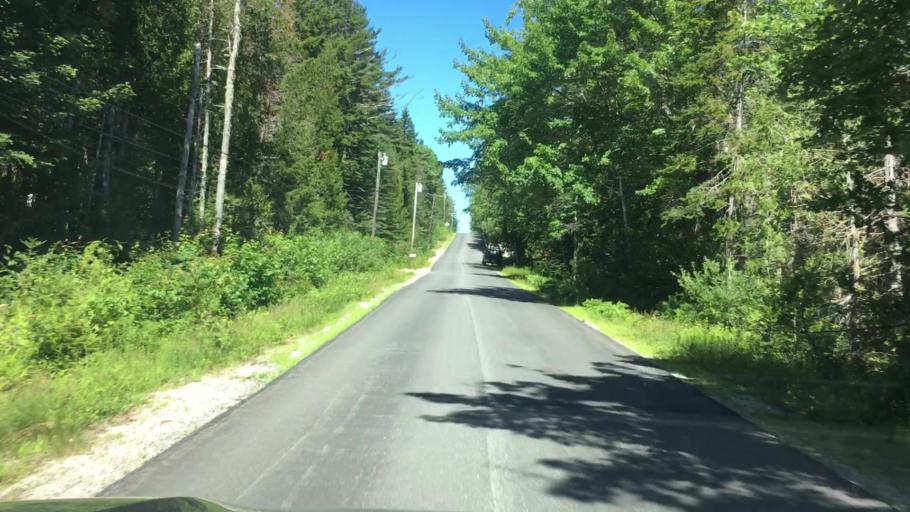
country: US
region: Maine
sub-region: Hancock County
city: Sedgwick
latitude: 44.3178
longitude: -68.6237
